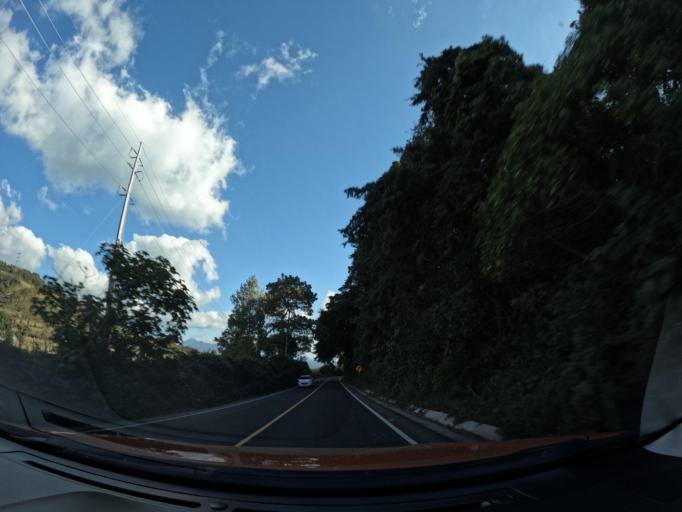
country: GT
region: Sacatepequez
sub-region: Municipio de Santa Maria de Jesus
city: Santa Maria de Jesus
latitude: 14.4769
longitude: -90.6948
